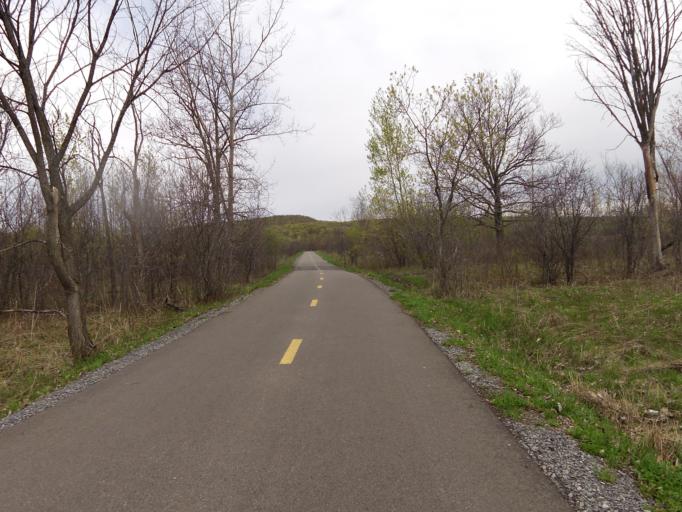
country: CA
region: Quebec
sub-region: Laurentides
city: Sainte-Marthe-sur-le-Lac
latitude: 45.4959
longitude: -73.9998
